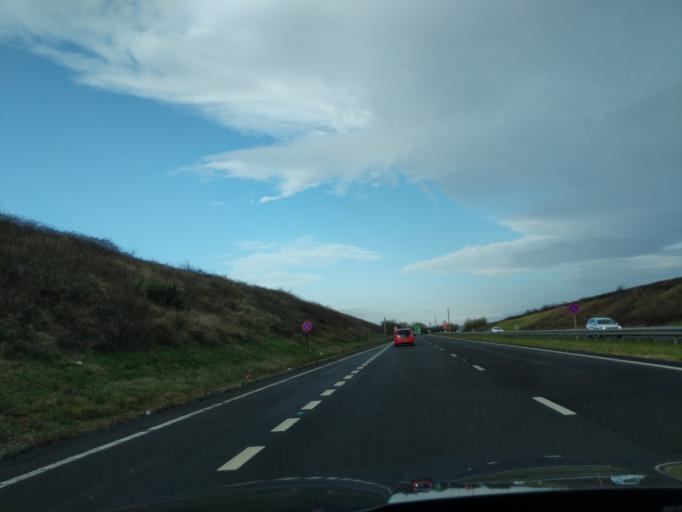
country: GB
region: England
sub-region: Northumberland
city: Ponteland
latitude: 55.0312
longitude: -1.7111
